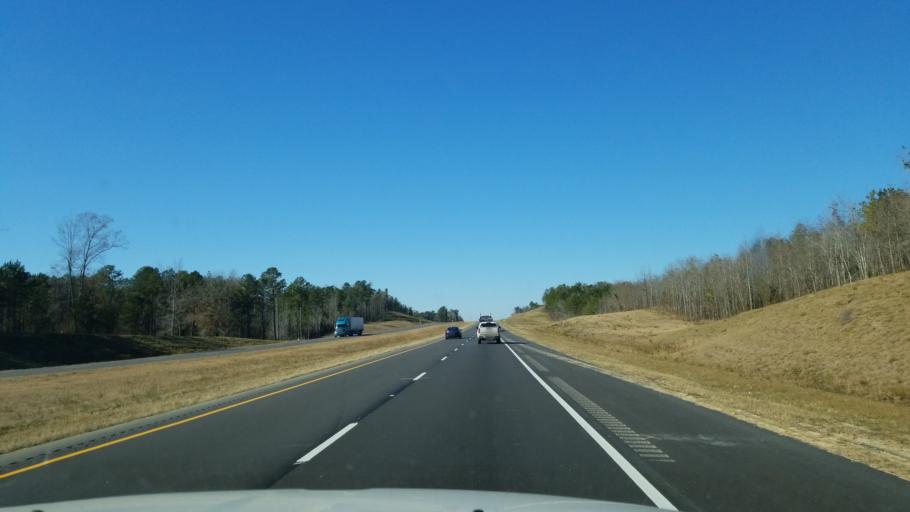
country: US
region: Alabama
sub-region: Pickens County
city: Reform
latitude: 33.3548
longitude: -87.9645
